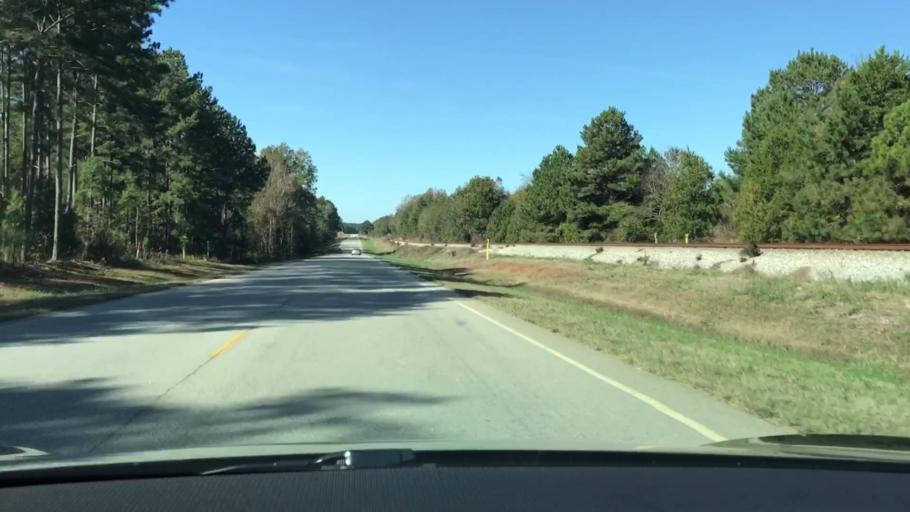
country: US
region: Georgia
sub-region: Warren County
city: Firing Range
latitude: 33.4818
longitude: -82.7691
